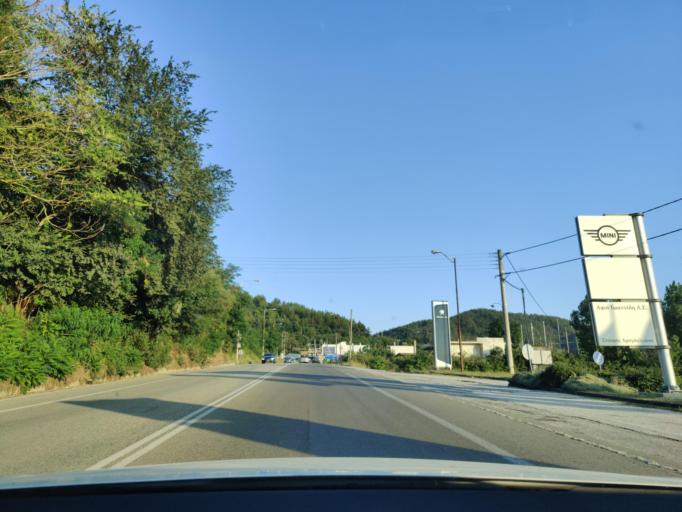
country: GR
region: East Macedonia and Thrace
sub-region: Nomos Kavalas
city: Amygdaleonas
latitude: 40.9530
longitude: 24.3677
